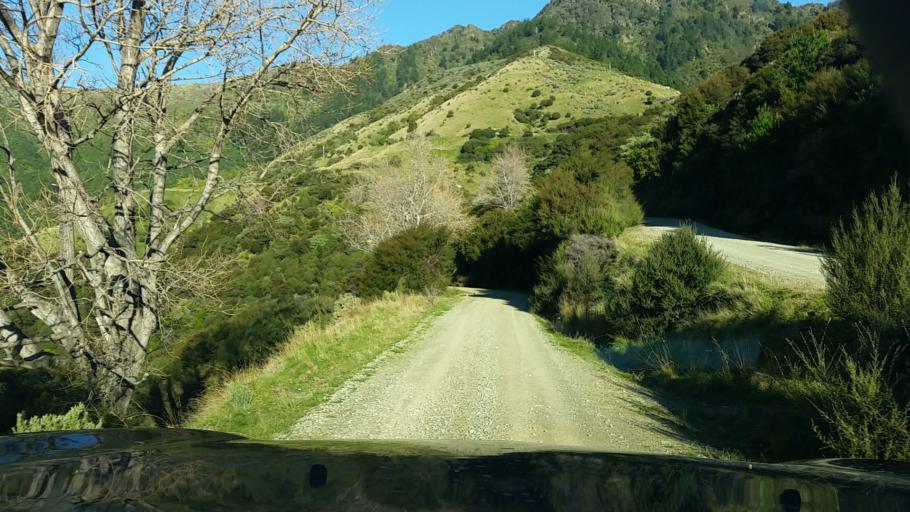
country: NZ
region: Marlborough
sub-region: Marlborough District
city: Picton
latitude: -41.0189
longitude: 174.1398
